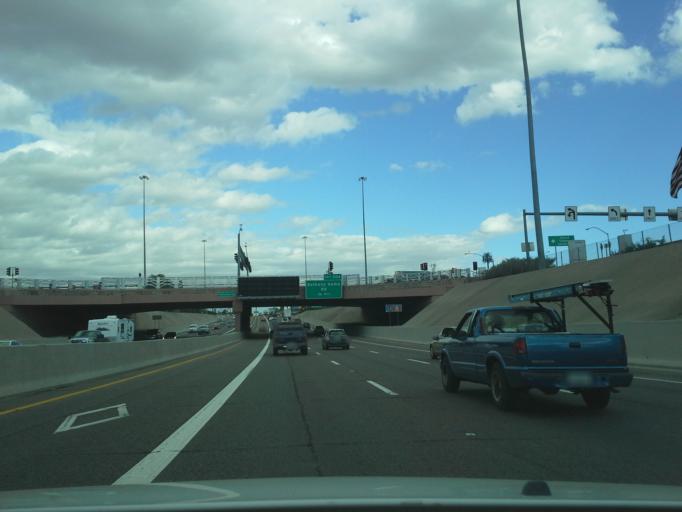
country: US
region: Arizona
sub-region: Maricopa County
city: Phoenix
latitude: 33.5083
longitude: -112.1124
